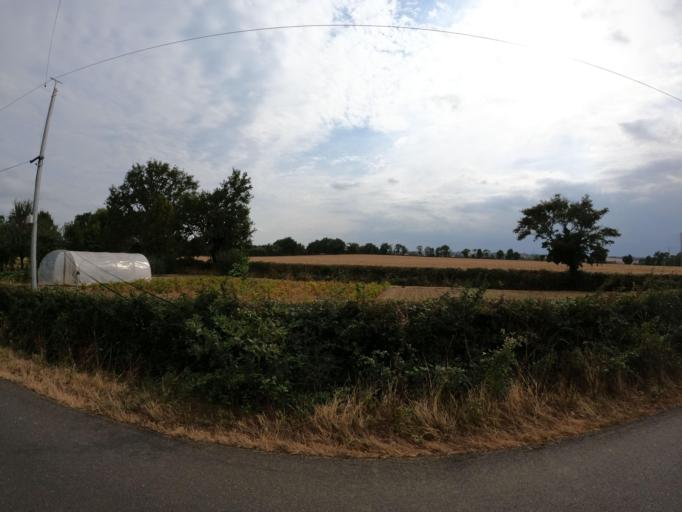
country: FR
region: Pays de la Loire
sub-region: Departement de Maine-et-Loire
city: Saint-Christophe-du-Bois
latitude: 47.0304
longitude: -0.9559
